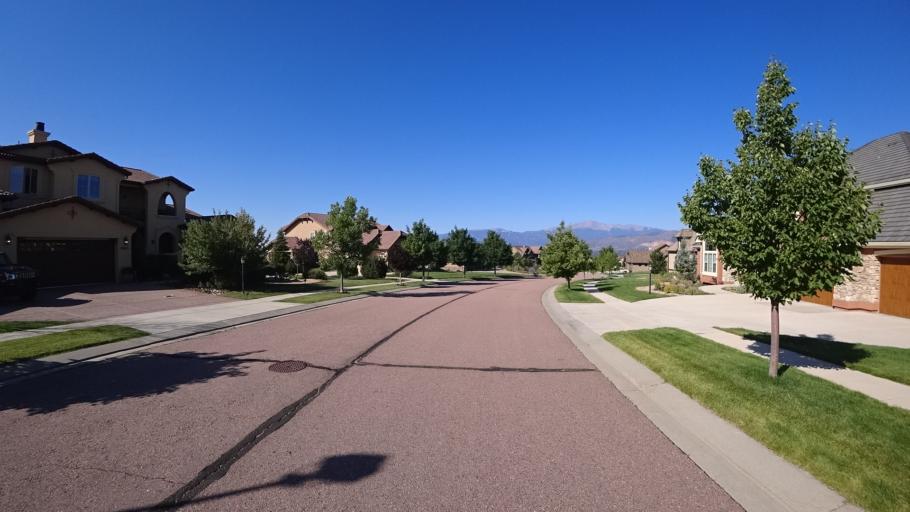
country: US
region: Colorado
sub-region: El Paso County
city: Black Forest
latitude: 38.9737
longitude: -104.7640
